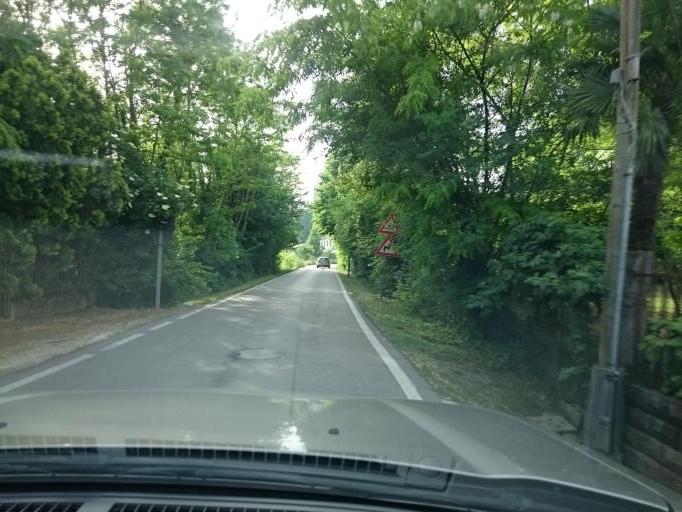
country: IT
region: Veneto
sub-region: Provincia di Venezia
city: Dolo
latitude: 45.4254
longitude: 12.0938
